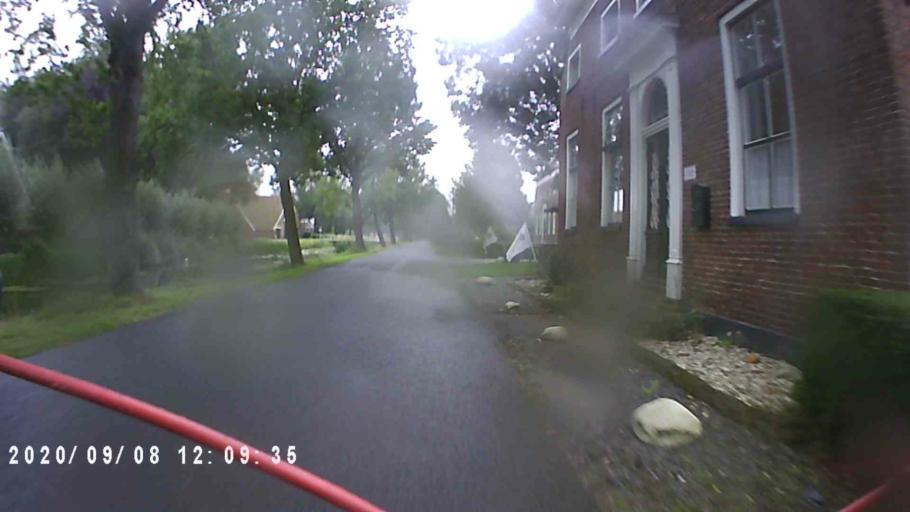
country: NL
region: Groningen
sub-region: Gemeente Veendam
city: Veendam
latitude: 53.0996
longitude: 6.8318
